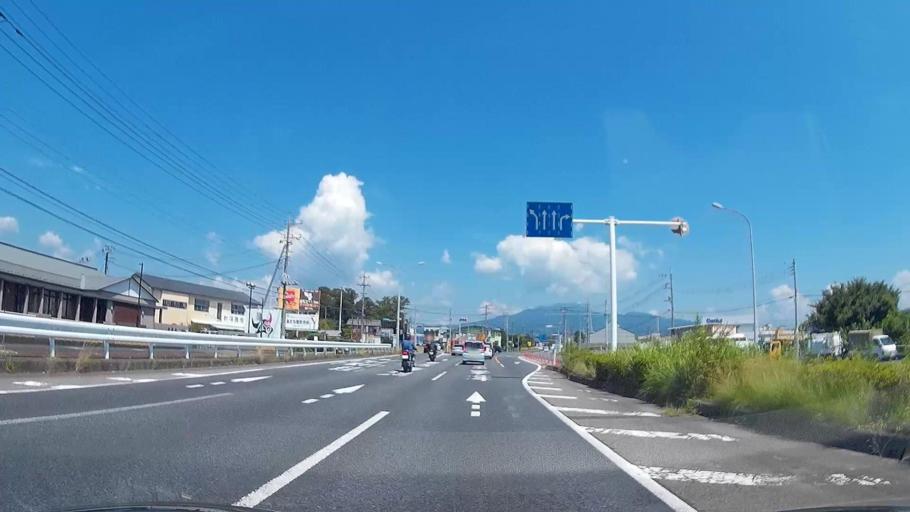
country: JP
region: Gunma
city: Shibukawa
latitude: 36.4843
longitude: 139.0126
